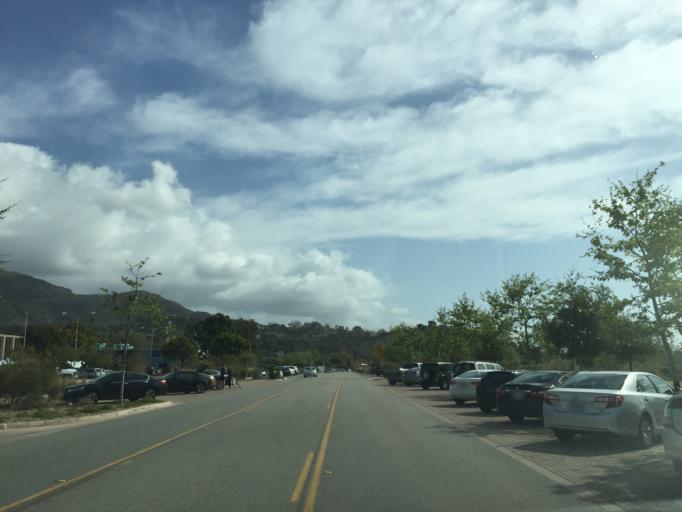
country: US
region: California
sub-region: Los Angeles County
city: Malibu Beach
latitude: 34.0361
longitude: -118.6898
